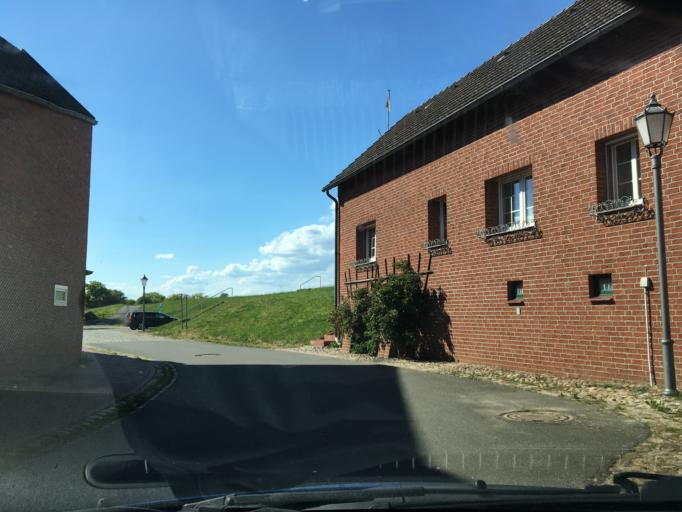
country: DE
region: Brandenburg
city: Lanz
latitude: 53.0380
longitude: 11.5663
